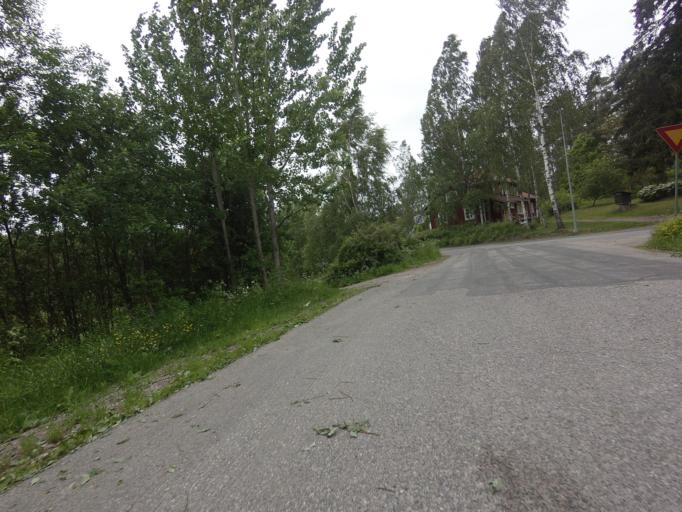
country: FI
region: Uusimaa
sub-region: Helsinki
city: Kauniainen
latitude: 60.1875
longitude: 24.7285
